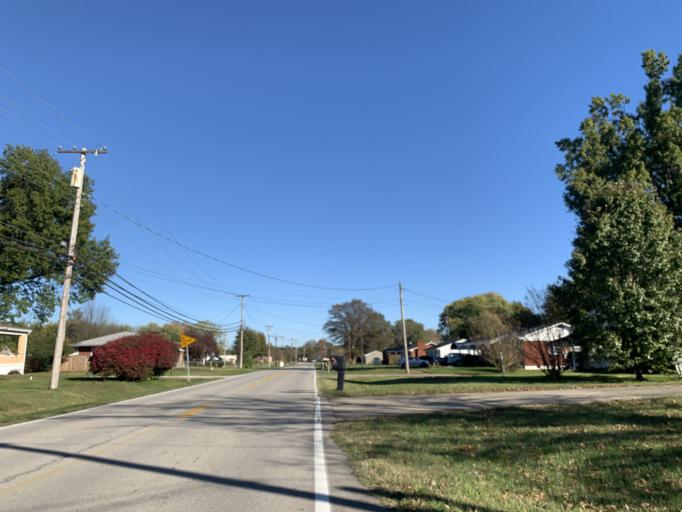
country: US
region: Kentucky
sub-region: Jefferson County
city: Pleasure Ridge Park
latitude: 38.1474
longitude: -85.8915
